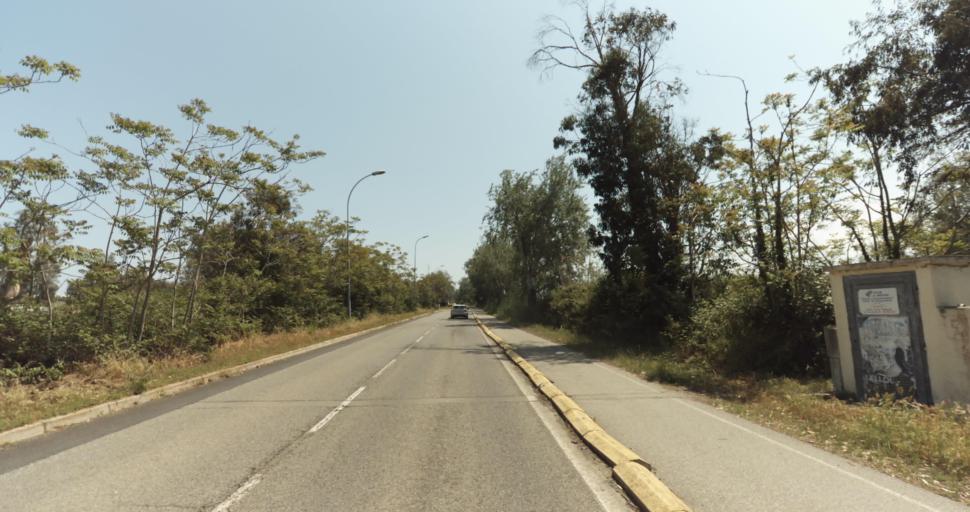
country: FR
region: Corsica
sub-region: Departement de la Haute-Corse
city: Biguglia
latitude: 42.6169
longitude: 9.4774
